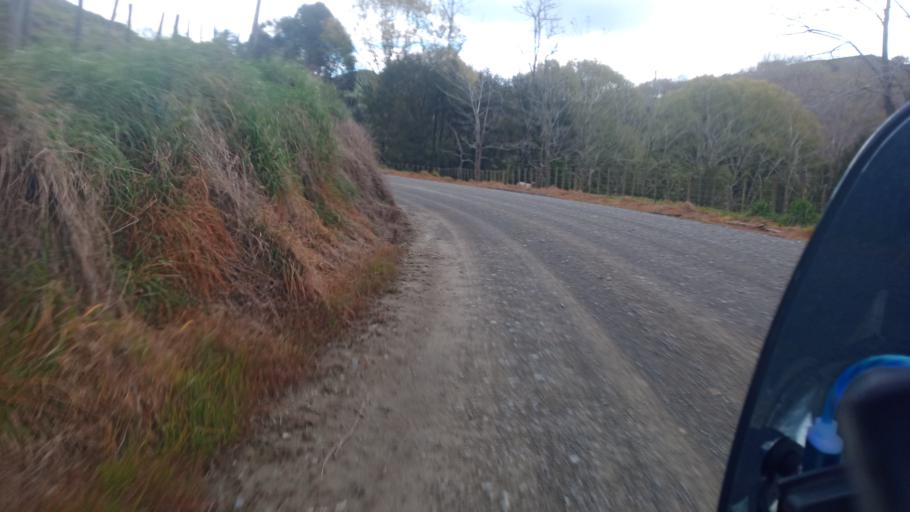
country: NZ
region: Gisborne
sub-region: Gisborne District
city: Gisborne
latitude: -38.2025
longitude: 178.2464
